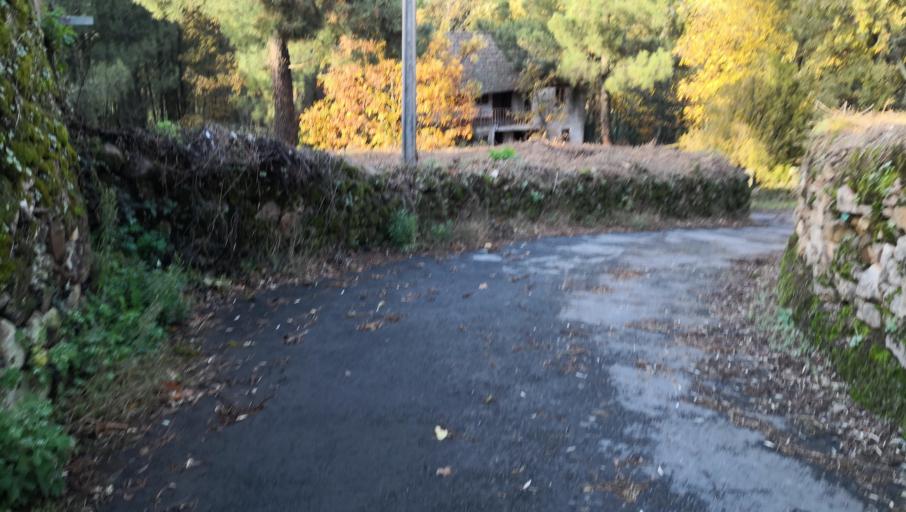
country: PT
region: Vila Real
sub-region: Vila Real
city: Vila Real
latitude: 41.3208
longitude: -7.7124
